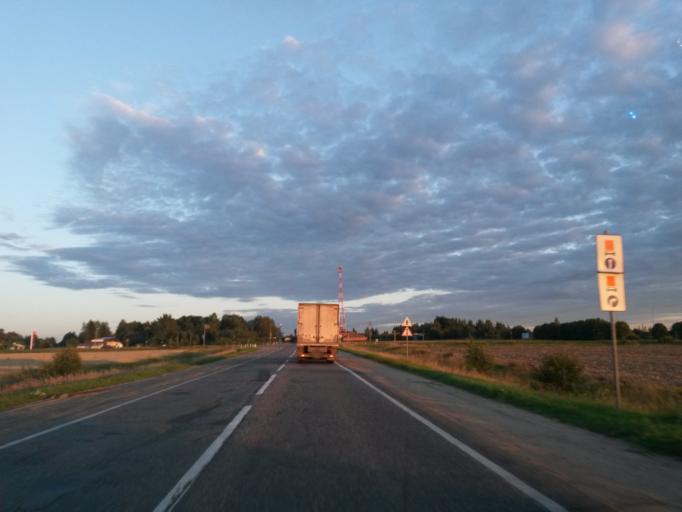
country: RU
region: Jaroslavl
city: Gavrilov-Yam
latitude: 57.3114
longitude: 39.9359
